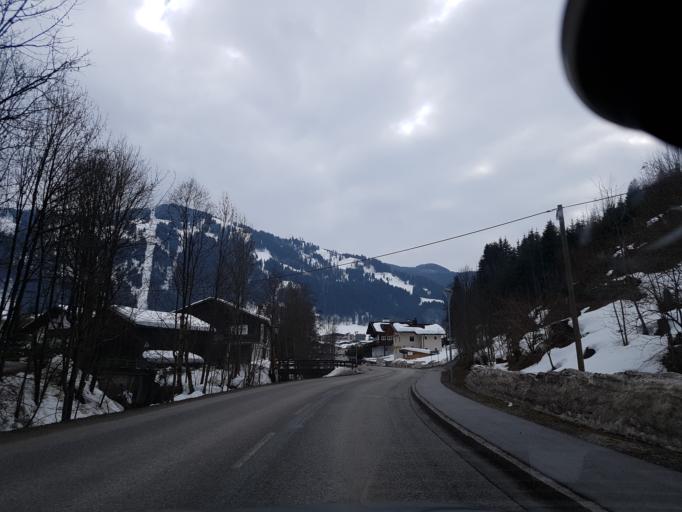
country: AT
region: Tyrol
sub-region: Politischer Bezirk Kufstein
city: Worgl
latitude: 47.4542
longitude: 12.0899
